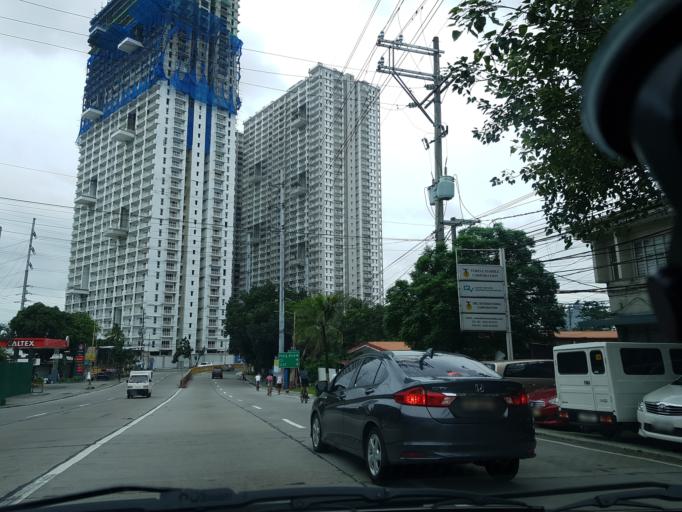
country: PH
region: Metro Manila
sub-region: Pasig
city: Pasig City
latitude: 14.5710
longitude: 121.0656
